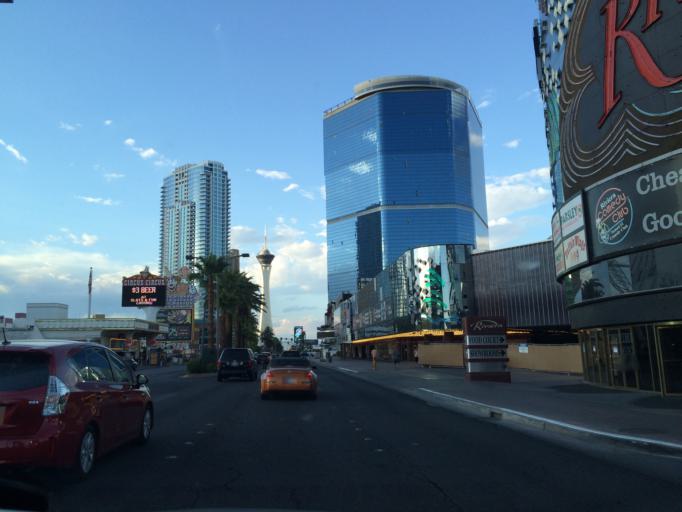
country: US
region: Nevada
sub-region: Clark County
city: Paradise
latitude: 36.1347
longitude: -115.1631
